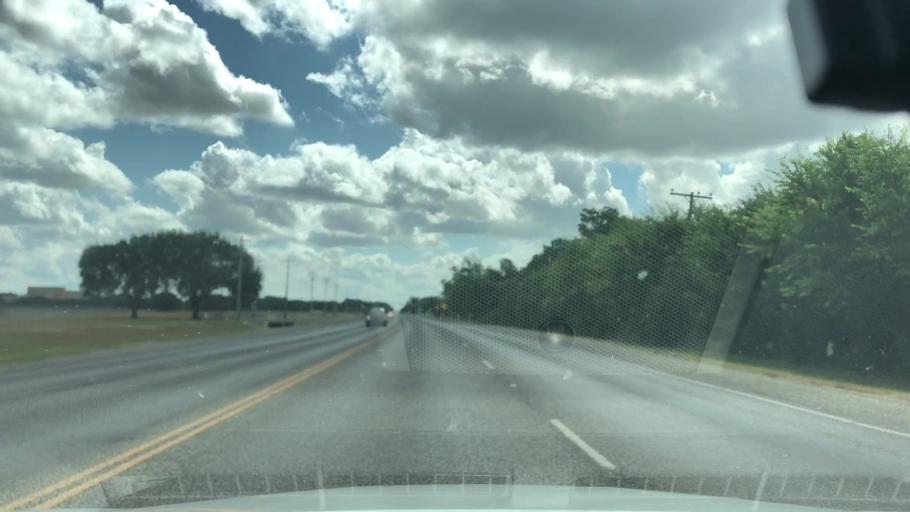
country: US
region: Texas
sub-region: Guadalupe County
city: Seguin
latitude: 29.5691
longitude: -97.9943
